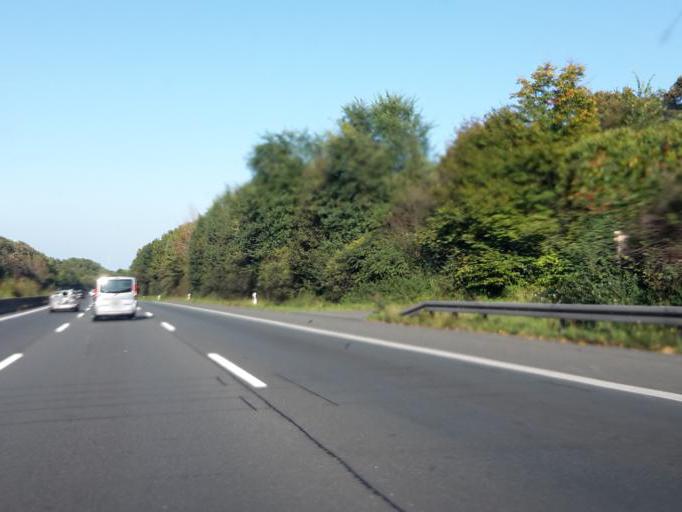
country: DE
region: North Rhine-Westphalia
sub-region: Regierungsbezirk Arnsberg
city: Holzwickede
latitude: 51.4869
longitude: 7.6260
